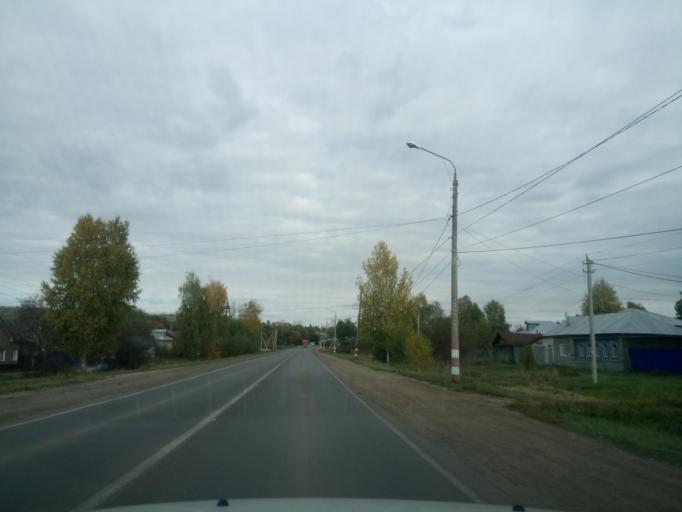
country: RU
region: Nizjnij Novgorod
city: Lukoyanov
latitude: 55.0304
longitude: 44.4759
